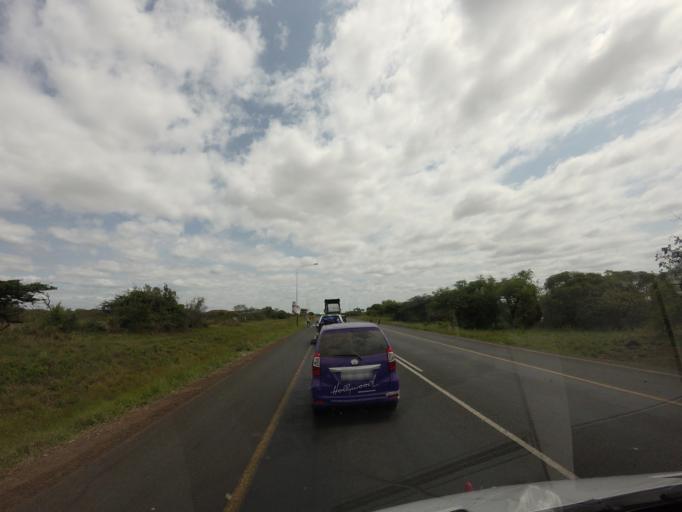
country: ZA
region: KwaZulu-Natal
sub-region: uMkhanyakude District Municipality
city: Hluhluwe
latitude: -28.0924
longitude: 32.2685
